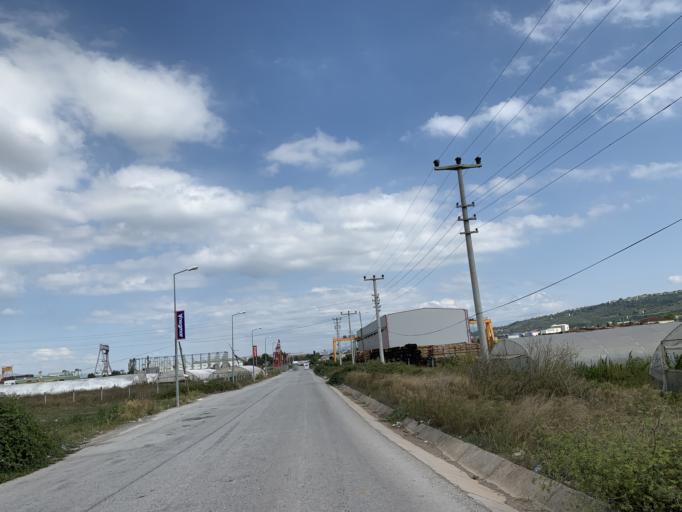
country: TR
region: Yalova
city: Taskopru
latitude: 40.6925
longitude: 29.4486
